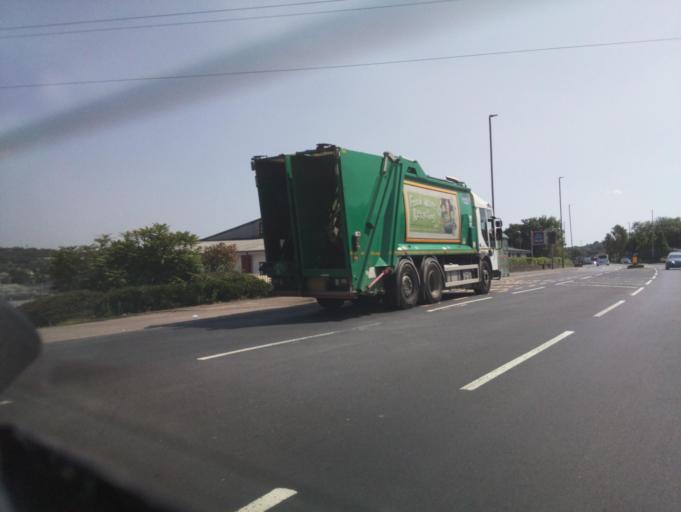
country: GB
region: Wales
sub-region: Caerphilly County Borough
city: Pengam
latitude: 51.6655
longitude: -3.2301
